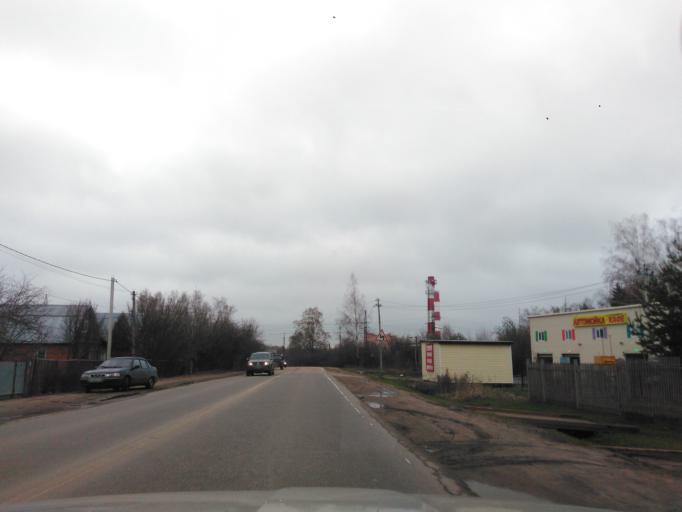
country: RU
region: Moskovskaya
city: Nakhabino
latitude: 55.8320
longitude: 37.1532
